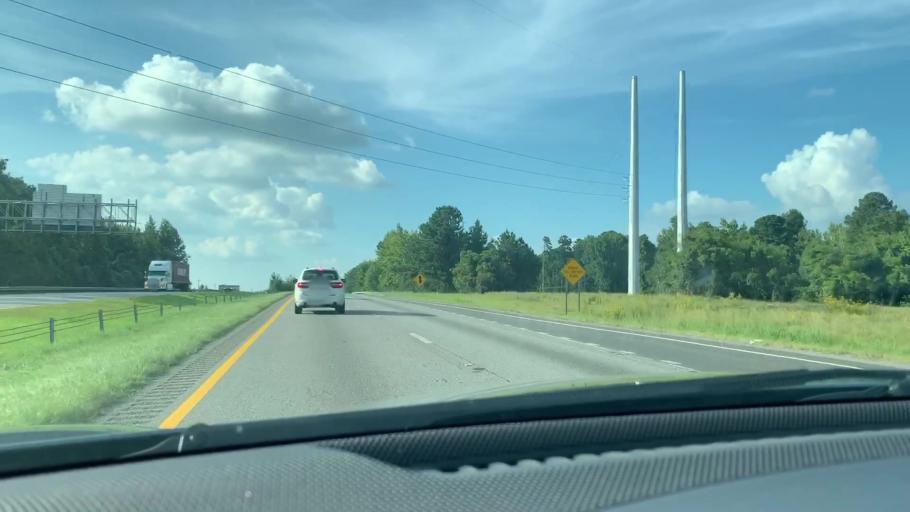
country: US
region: South Carolina
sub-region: Orangeburg County
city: Brookdale
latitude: 33.5602
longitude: -80.8254
